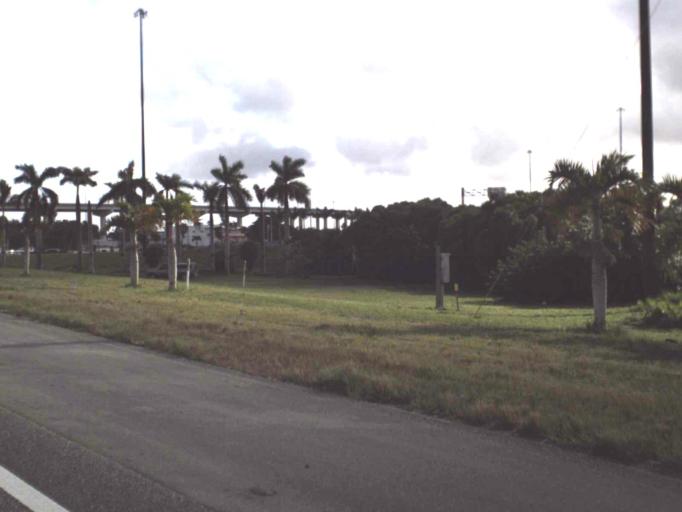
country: US
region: Florida
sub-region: Miami-Dade County
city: Norland
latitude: 25.9313
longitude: -80.2121
